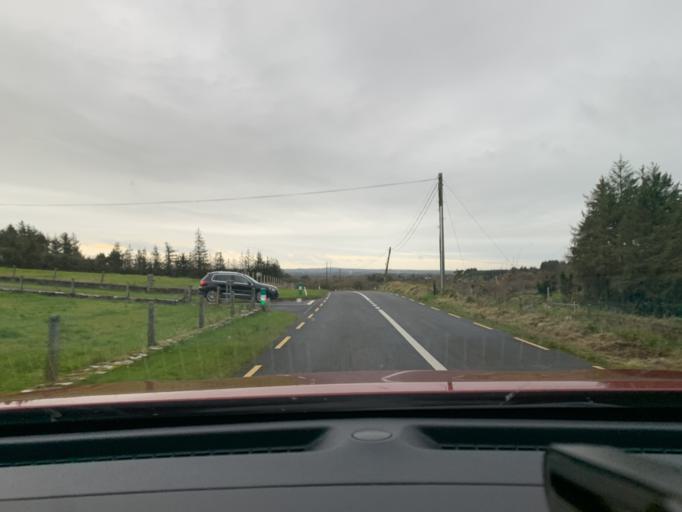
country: IE
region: Connaught
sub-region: Roscommon
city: Ballaghaderreen
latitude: 53.9425
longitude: -8.5450
